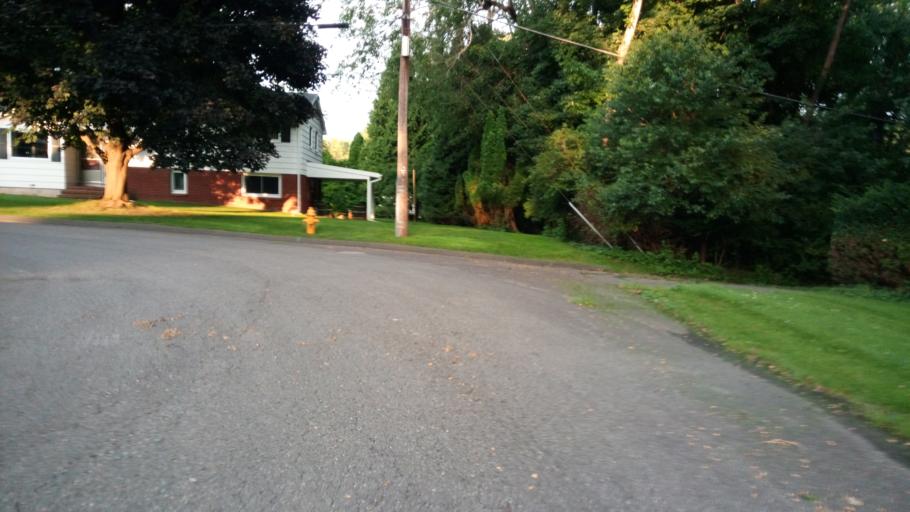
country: US
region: New York
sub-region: Chemung County
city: West Elmira
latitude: 42.0756
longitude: -76.8516
